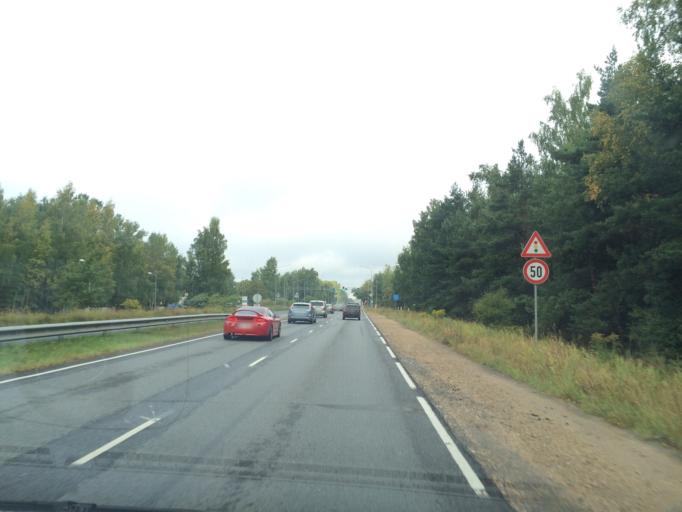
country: LV
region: Kekava
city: Kekava
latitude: 56.8692
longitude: 24.2768
